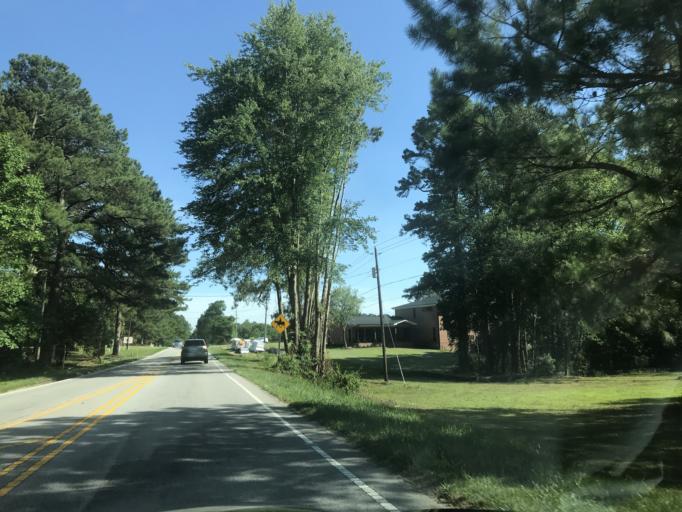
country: US
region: North Carolina
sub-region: Wake County
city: Garner
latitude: 35.6852
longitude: -78.5803
